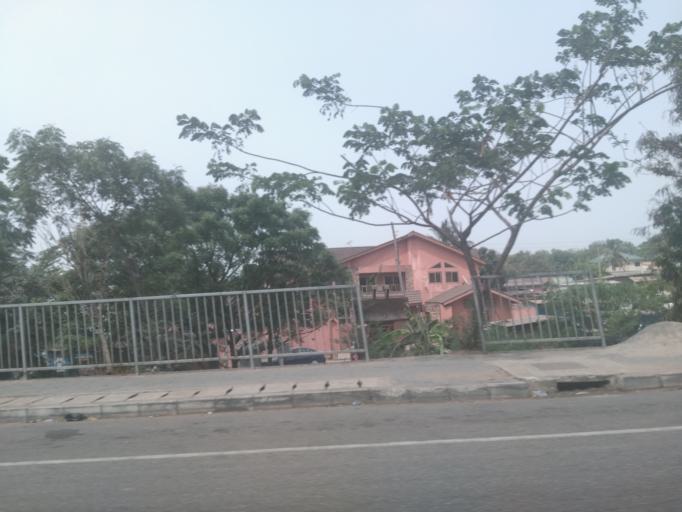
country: GH
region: Greater Accra
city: Dome
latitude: 5.6134
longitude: -0.2247
